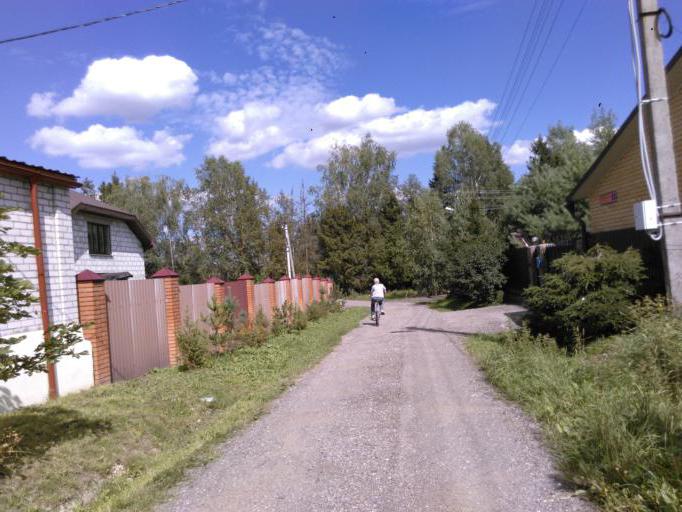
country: RU
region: Moskovskaya
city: Solnechnogorsk
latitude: 56.1332
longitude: 36.9210
